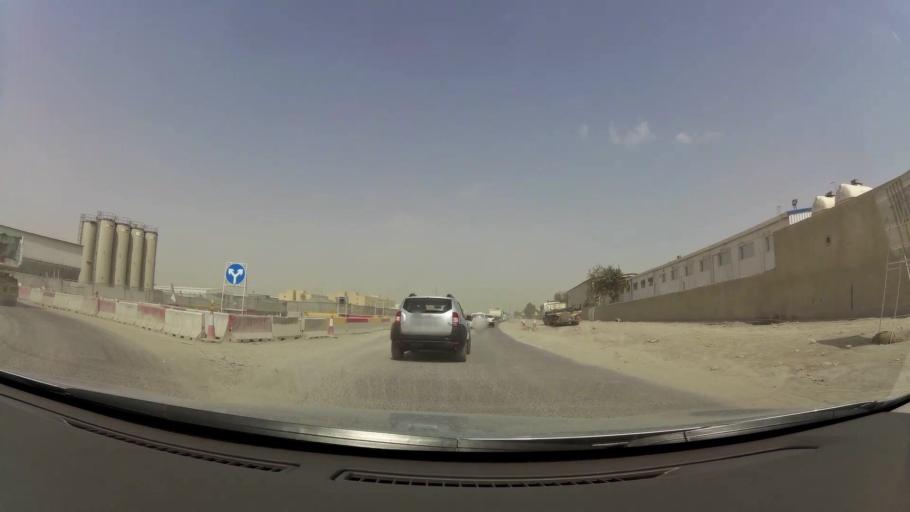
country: QA
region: Al Wakrah
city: Al Wukayr
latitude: 25.1762
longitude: 51.4459
